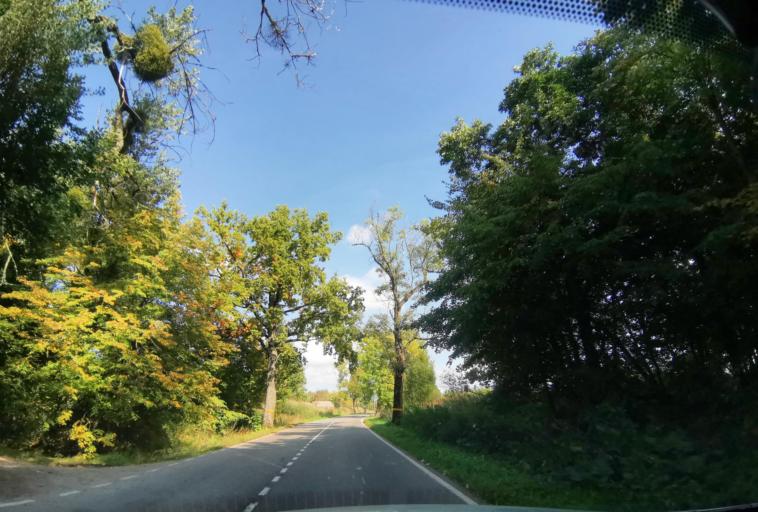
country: PL
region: Warmian-Masurian Voivodeship
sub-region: Powiat goldapski
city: Goldap
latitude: 54.4594
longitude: 22.3811
